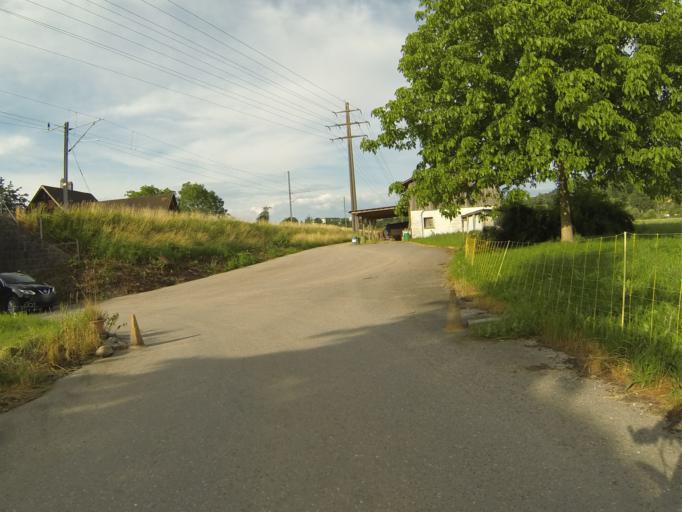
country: CH
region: Lucerne
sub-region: Lucerne-Stadt District
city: Littau
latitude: 47.0570
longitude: 8.2626
